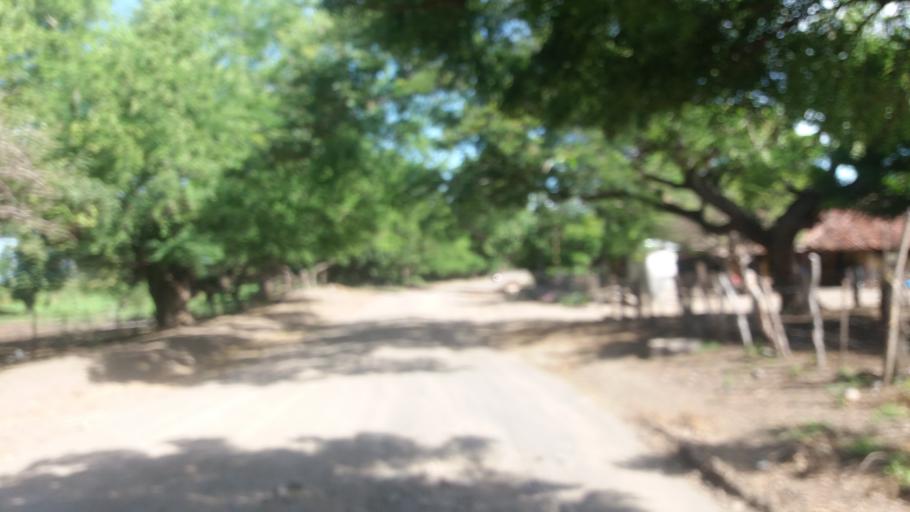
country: NI
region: Granada
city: Granada
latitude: 12.0031
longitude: -85.9346
